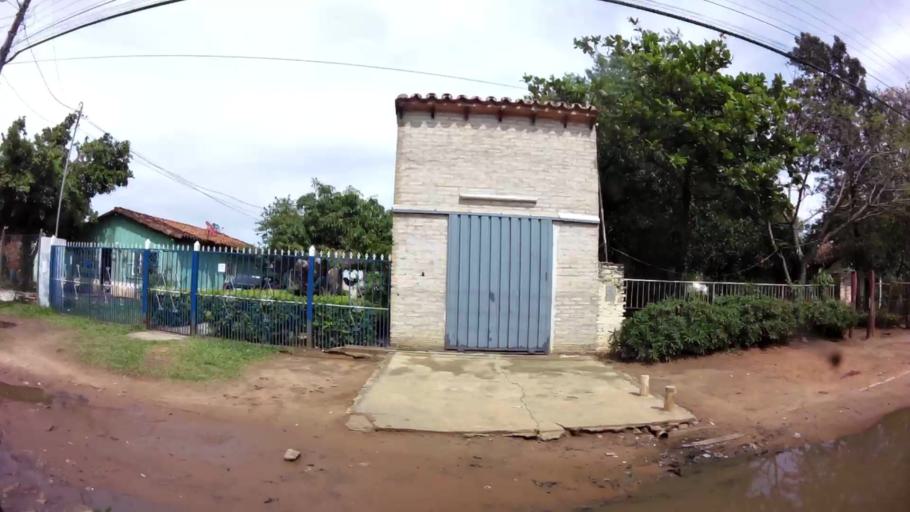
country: PY
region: Central
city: Limpio
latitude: -25.1879
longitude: -57.4775
